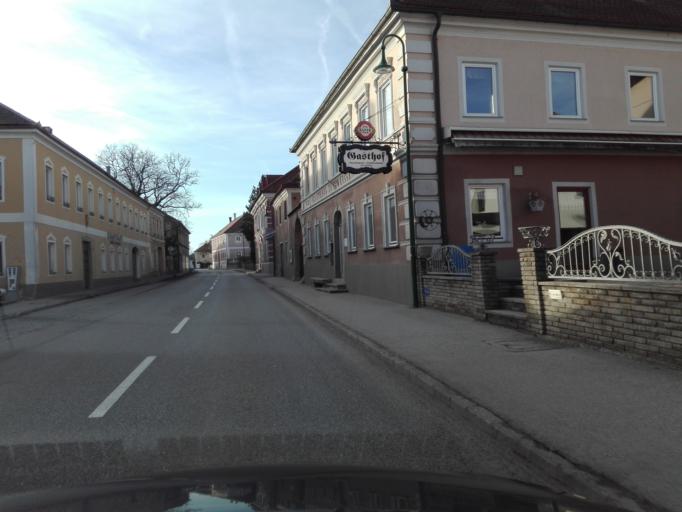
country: AT
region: Lower Austria
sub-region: Politischer Bezirk Amstetten
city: Strengberg
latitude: 48.1429
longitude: 14.6512
